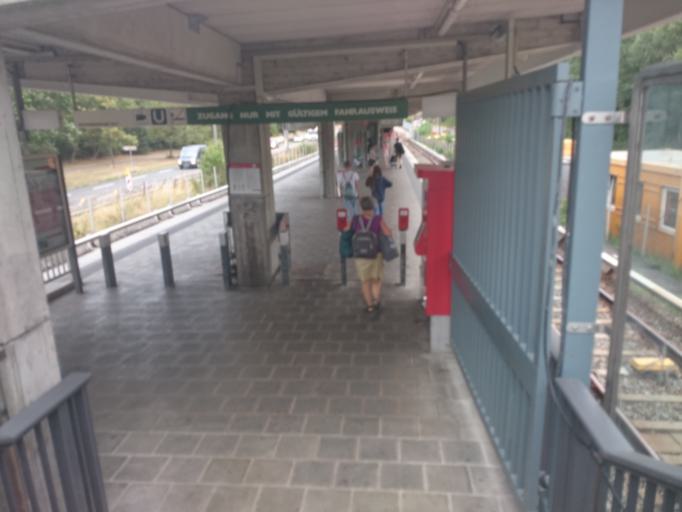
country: DE
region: Bavaria
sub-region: Regierungsbezirk Mittelfranken
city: Nuernberg
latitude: 49.4129
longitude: 11.1210
